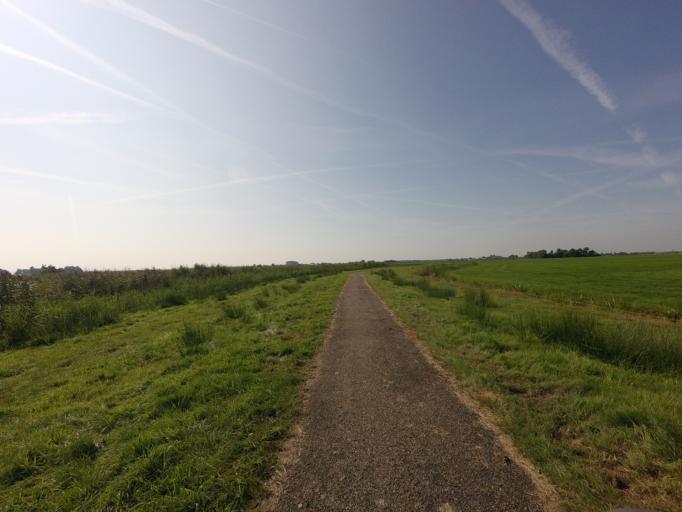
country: NL
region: Overijssel
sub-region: Gemeente Steenwijkerland
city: Oldemarkt
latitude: 52.8389
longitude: 5.9560
